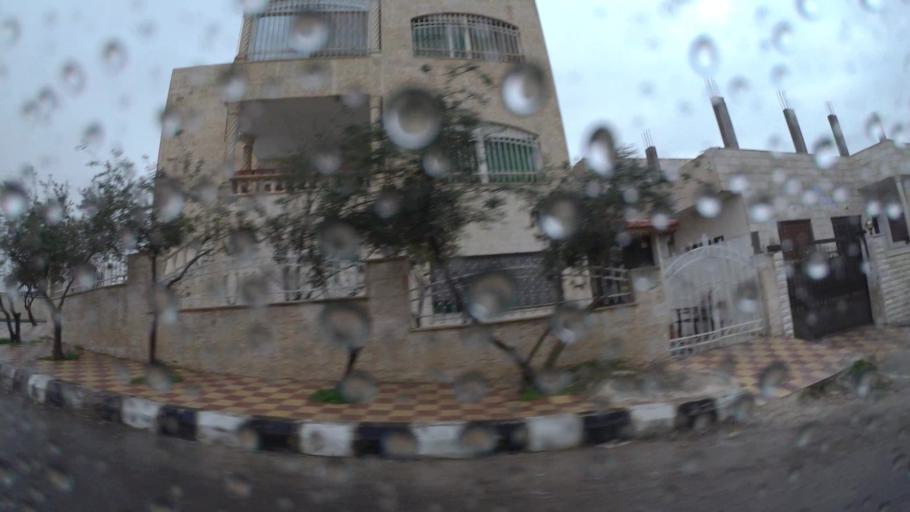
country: JO
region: Amman
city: Amman
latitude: 32.0031
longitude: 35.9598
